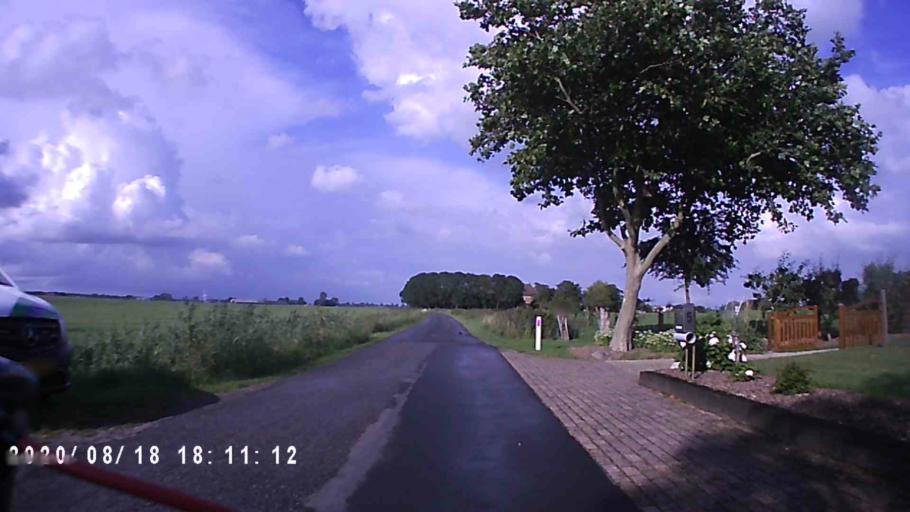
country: NL
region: Groningen
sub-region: Gemeente Zuidhorn
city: Oldehove
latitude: 53.2830
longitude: 6.4133
